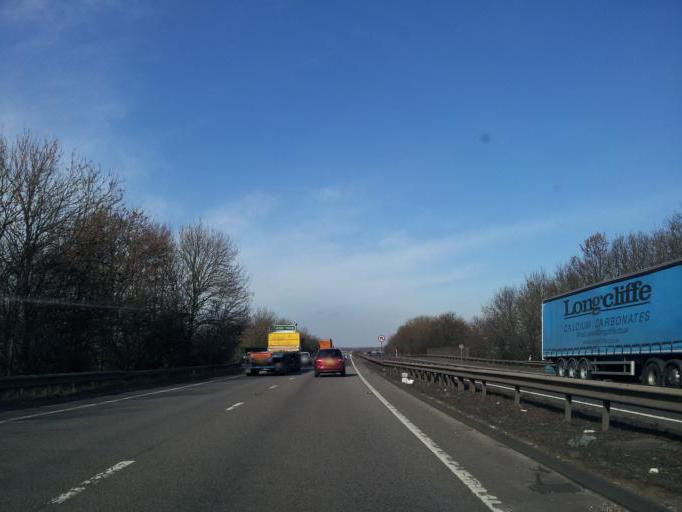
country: GB
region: England
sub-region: Lincolnshire
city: Great Gonerby
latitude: 52.9381
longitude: -0.6852
